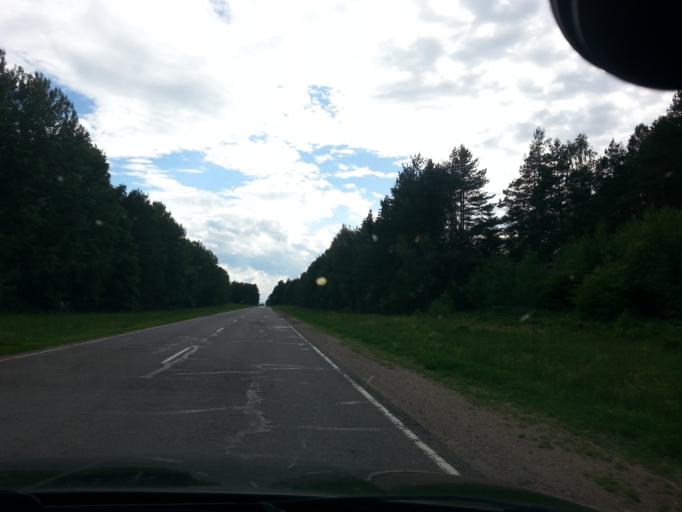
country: BY
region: Grodnenskaya
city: Astravyets
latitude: 54.7939
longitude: 26.0973
